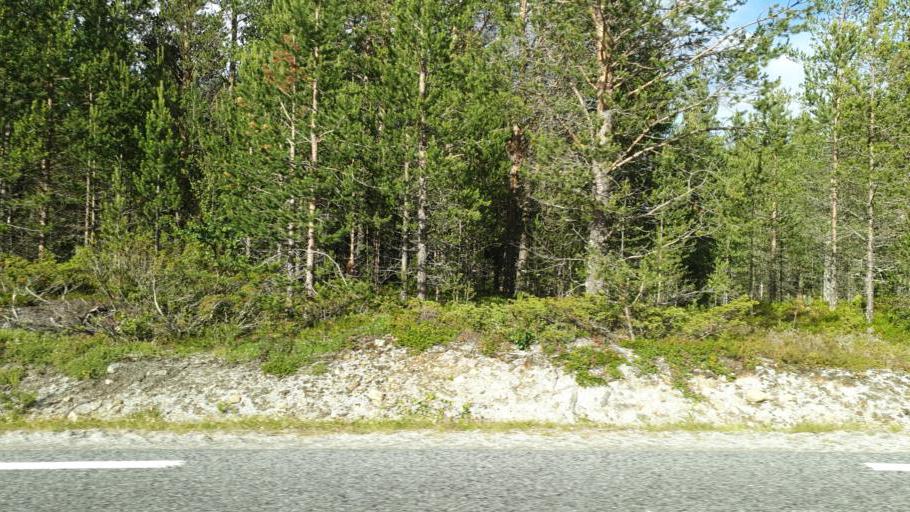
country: NO
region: Oppland
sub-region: Vaga
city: Vagamo
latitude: 61.8237
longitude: 8.9724
